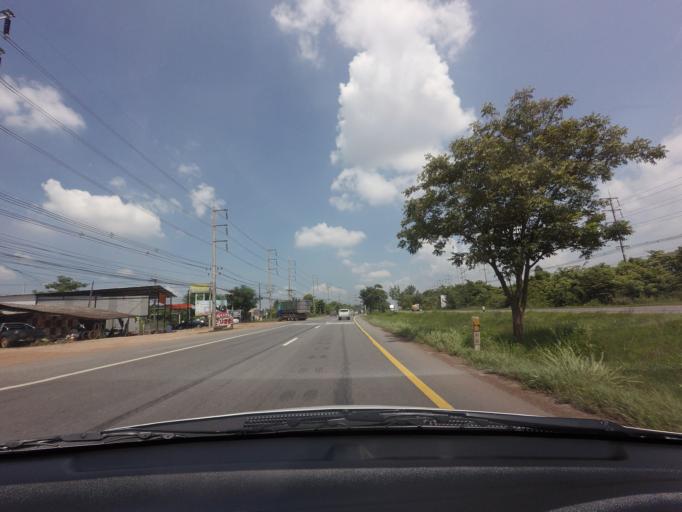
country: TH
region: Prachin Buri
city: Si Maha Phot
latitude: 13.8850
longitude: 101.5664
